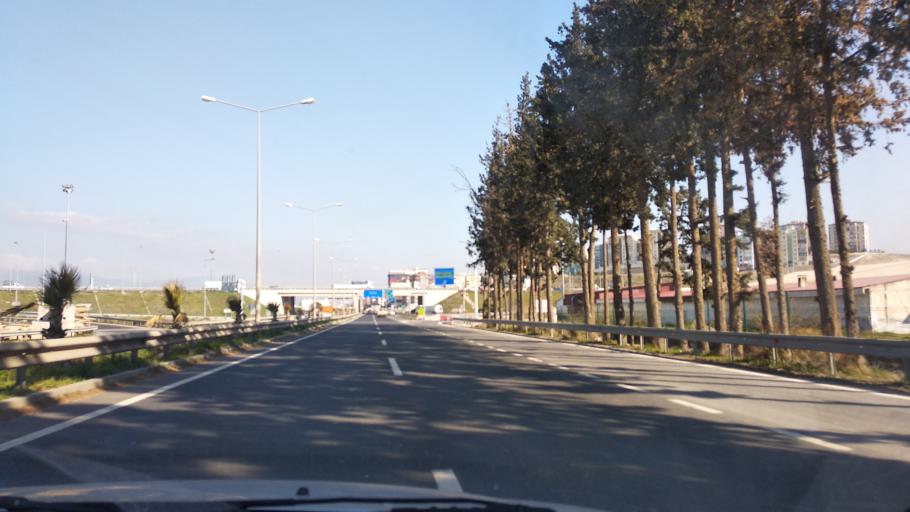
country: TR
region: Izmir
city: Menemen
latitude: 38.5689
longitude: 27.0547
